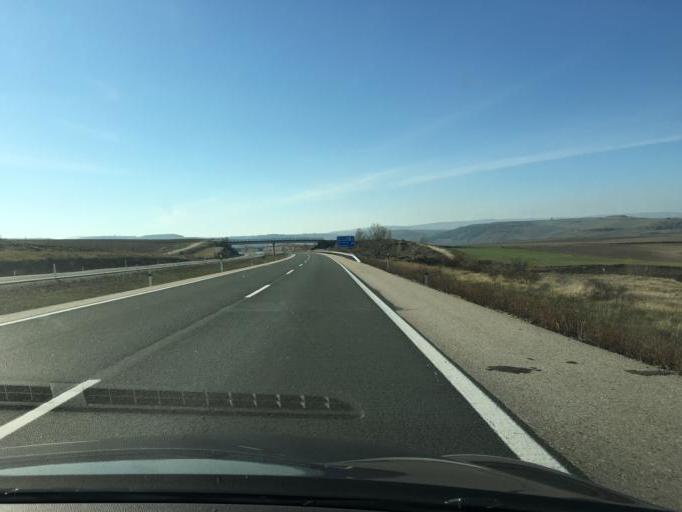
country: ES
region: Castille and Leon
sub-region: Provincia de Burgos
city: Briviesca
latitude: 42.5396
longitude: -3.3032
